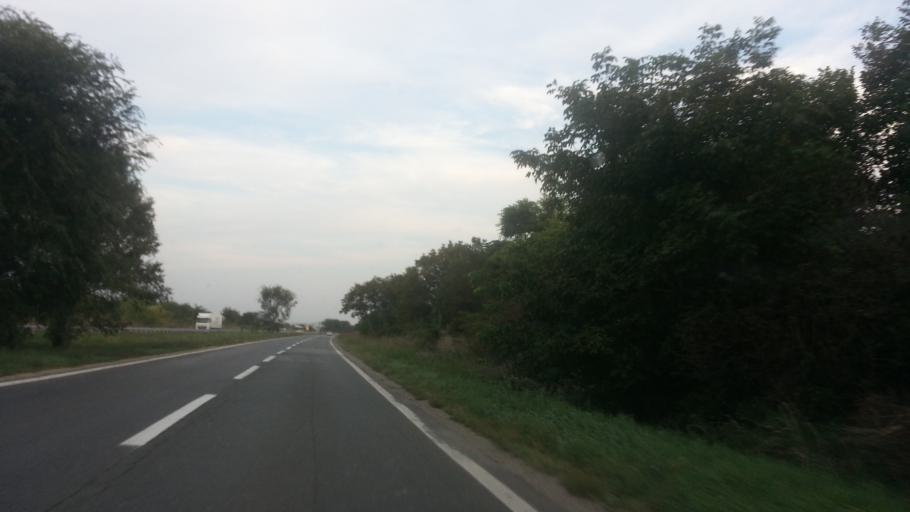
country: RS
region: Central Serbia
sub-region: Belgrade
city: Zemun
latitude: 44.8778
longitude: 20.3246
